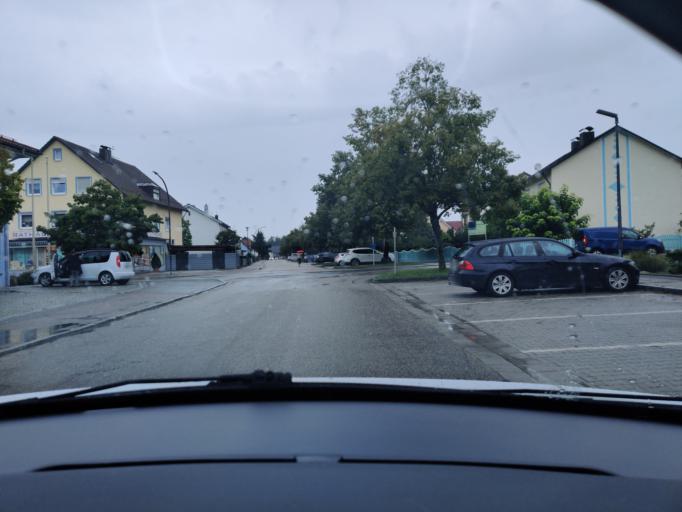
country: DE
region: Bavaria
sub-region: Upper Palatinate
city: Schwarzenfeld
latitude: 49.3899
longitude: 12.1348
